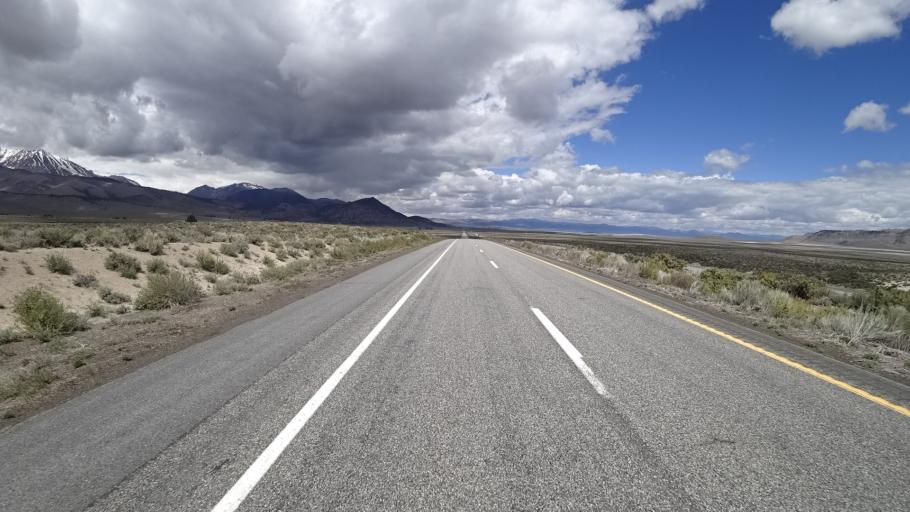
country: US
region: California
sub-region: Mono County
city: Mammoth Lakes
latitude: 37.8677
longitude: -119.0876
